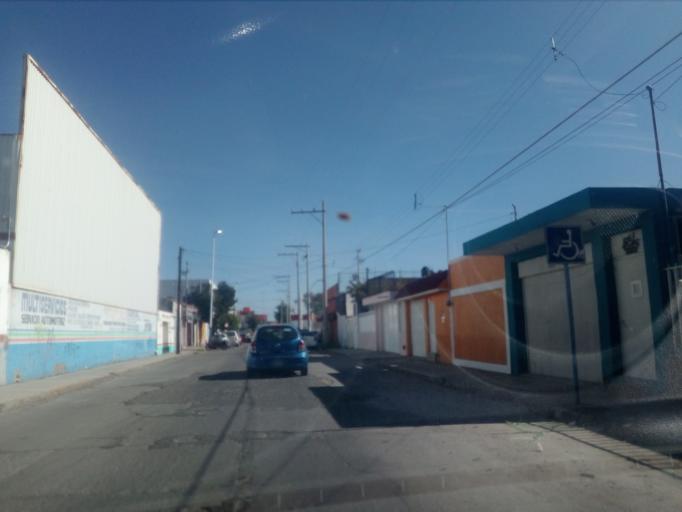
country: MX
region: Durango
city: Victoria de Durango
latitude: 24.0048
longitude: -104.6578
